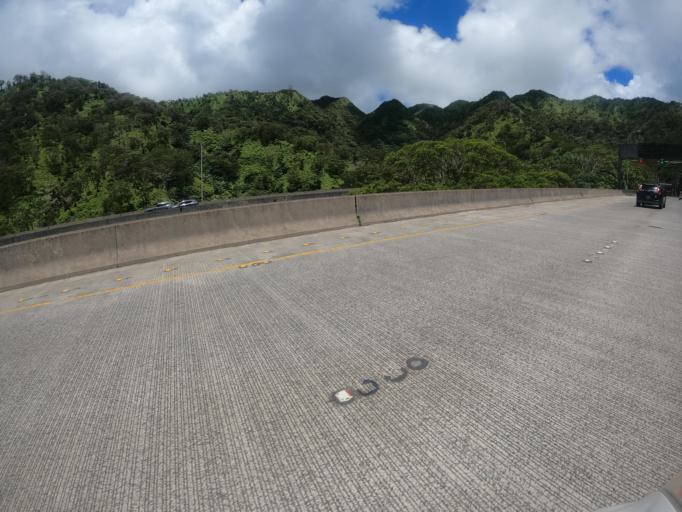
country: US
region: Hawaii
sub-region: Honolulu County
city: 'Ahuimanu
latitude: 21.4055
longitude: -157.8535
